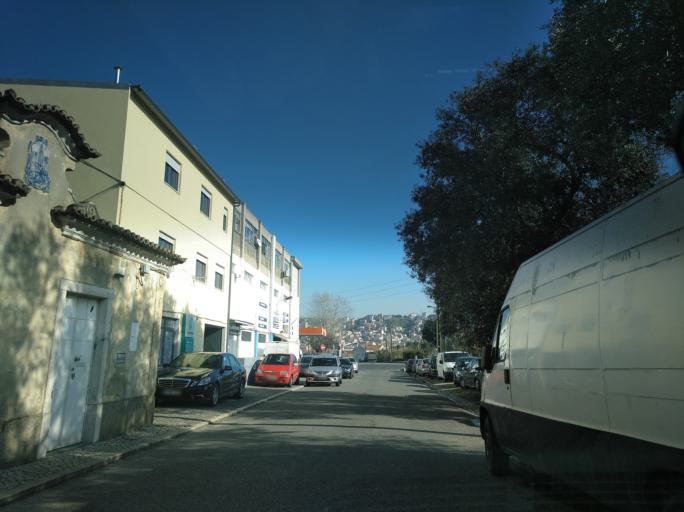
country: PT
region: Lisbon
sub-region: Odivelas
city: Pontinha
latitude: 38.7781
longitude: -9.2025
